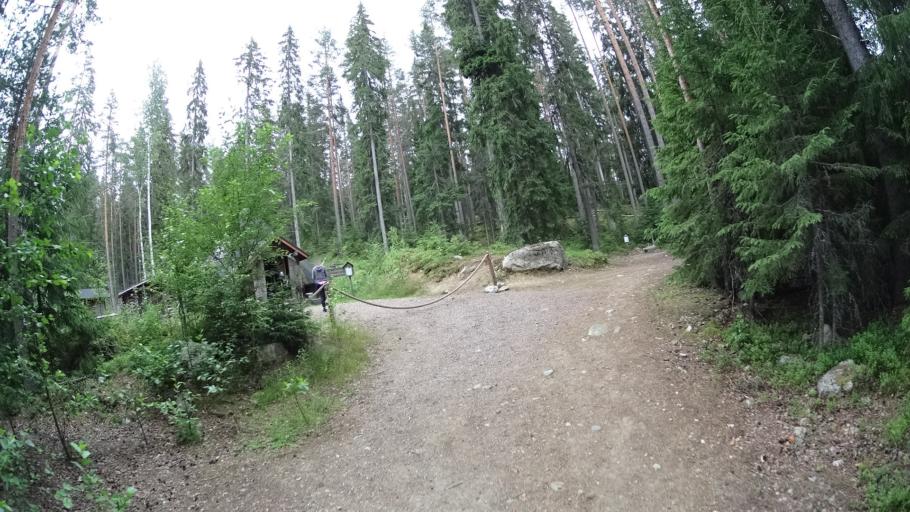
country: FI
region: Southern Savonia
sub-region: Mikkeli
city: Maentyharju
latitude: 61.1775
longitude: 26.8965
